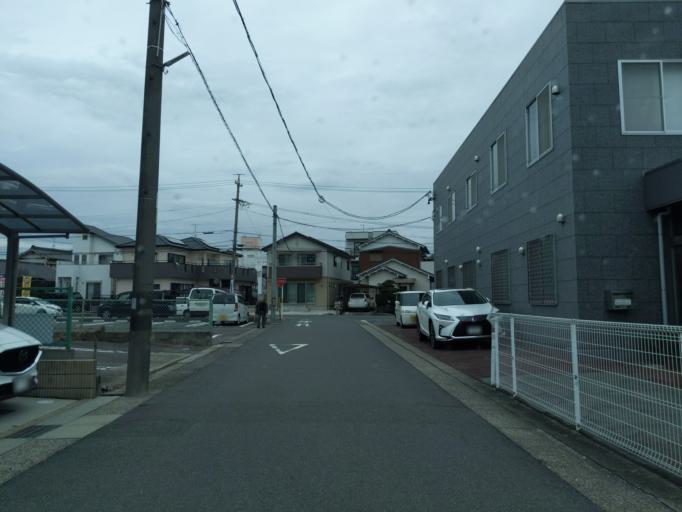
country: JP
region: Aichi
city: Kasugai
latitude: 35.2605
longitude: 136.9880
